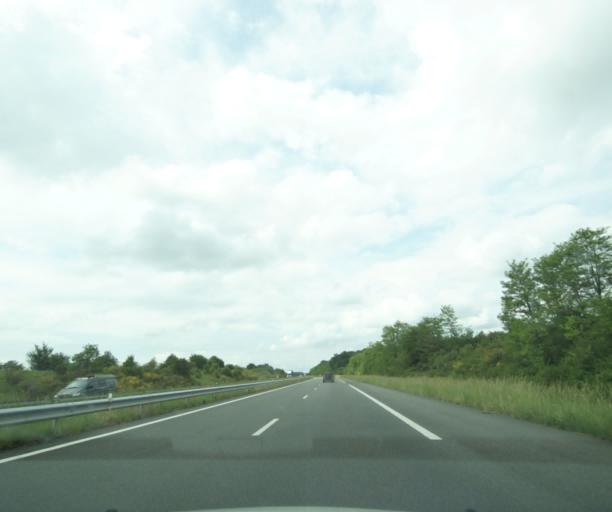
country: FR
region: Centre
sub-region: Departement du Cher
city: Orval
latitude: 46.7946
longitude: 2.4138
